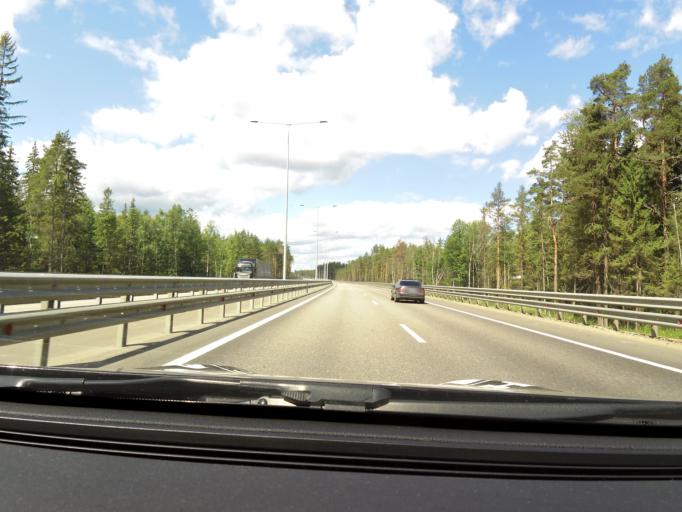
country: RU
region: Tverskaya
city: Vydropuzhsk
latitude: 57.2744
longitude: 34.8494
